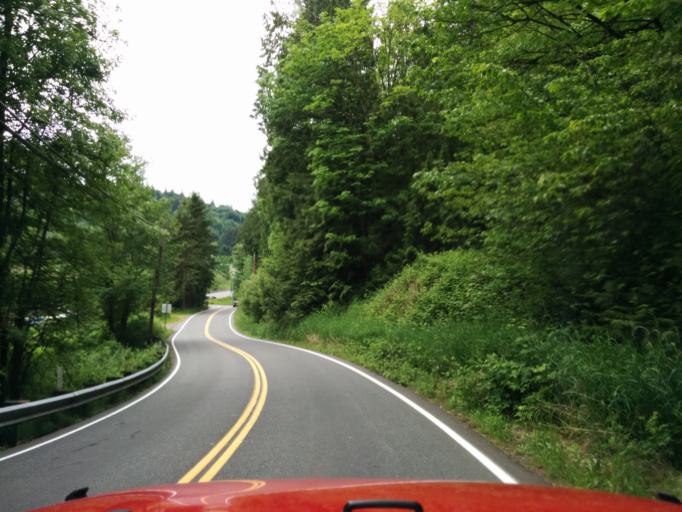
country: US
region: Washington
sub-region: King County
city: Sammamish
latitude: 47.6582
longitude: -122.0694
